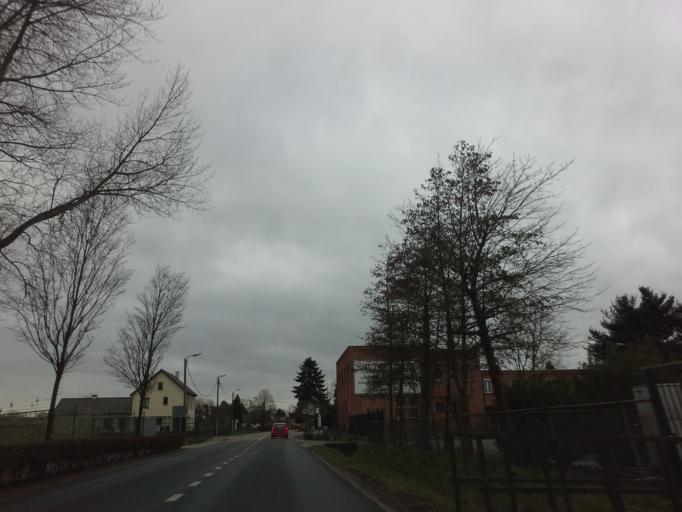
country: BE
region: Flanders
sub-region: Provincie Antwerpen
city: Hulshout
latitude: 51.1119
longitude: 4.8075
